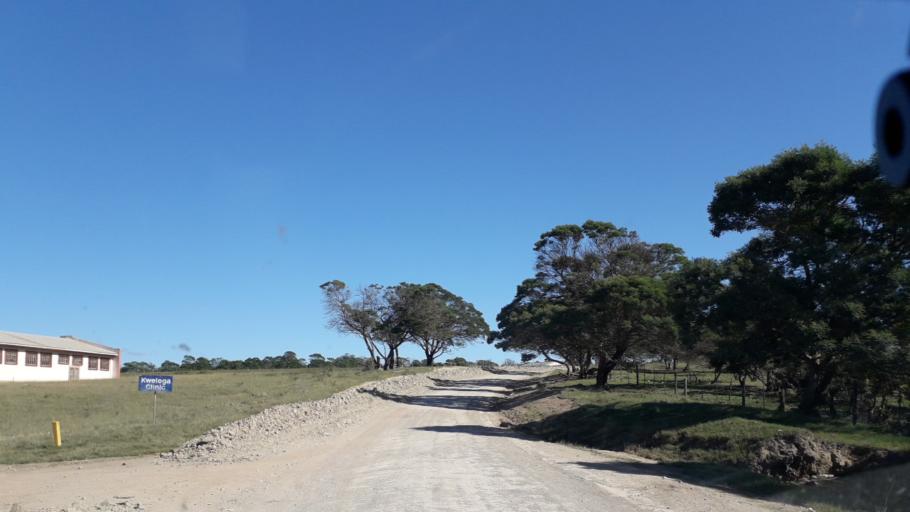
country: ZA
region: Eastern Cape
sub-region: Buffalo City Metropolitan Municipality
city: East London
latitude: -32.8215
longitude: 27.9631
